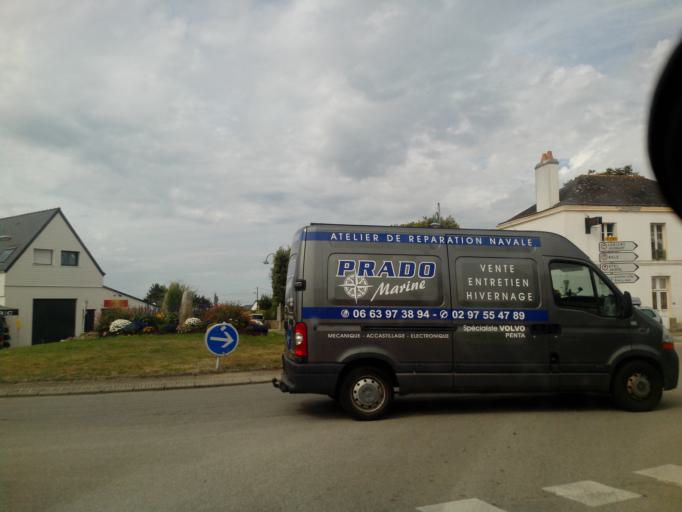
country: FR
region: Brittany
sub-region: Departement du Morbihan
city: Erdeven
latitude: 47.6396
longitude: -3.1537
